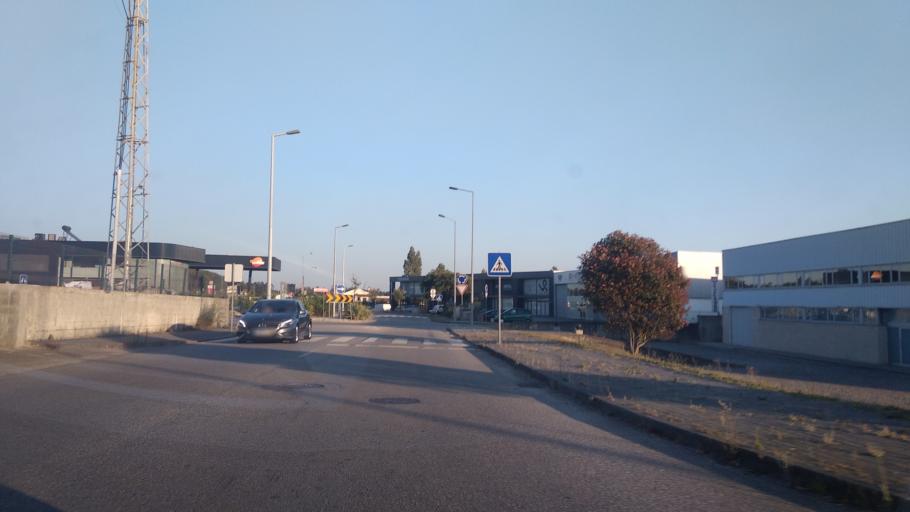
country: PT
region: Braga
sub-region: Esposende
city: Esposende
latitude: 41.5309
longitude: -8.7638
